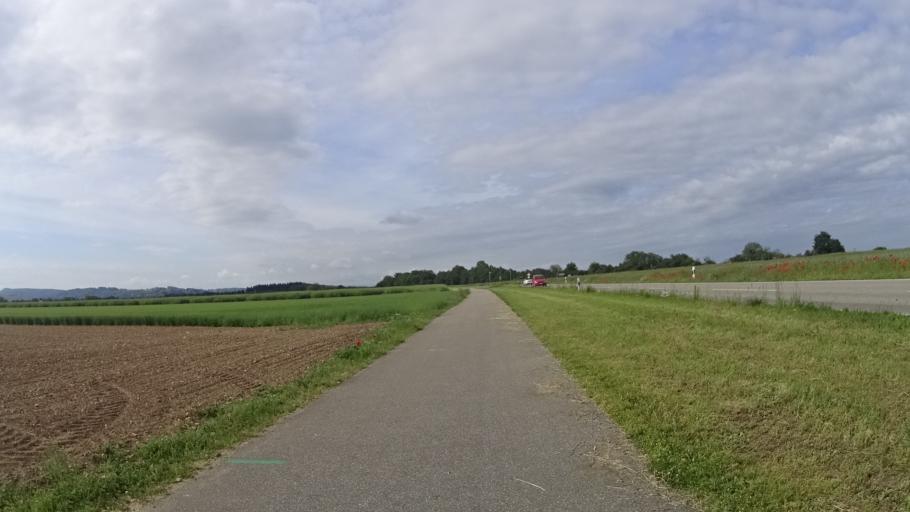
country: DE
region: Baden-Wuerttemberg
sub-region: Freiburg Region
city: Neuenburg am Rhein
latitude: 47.7964
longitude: 7.5569
